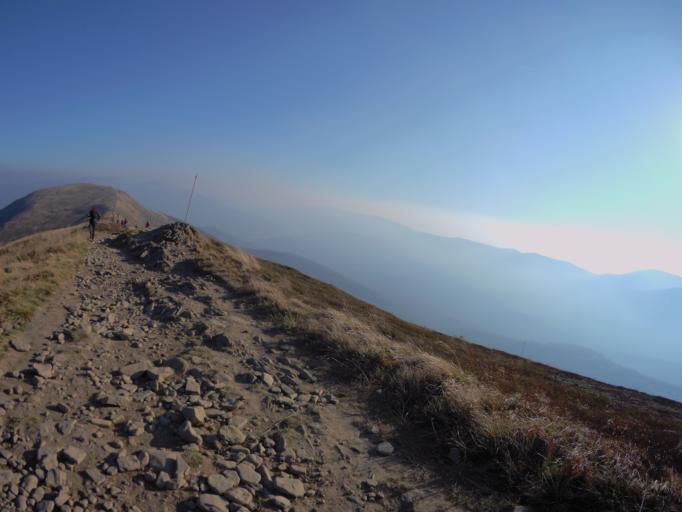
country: PL
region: Subcarpathian Voivodeship
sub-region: Powiat bieszczadzki
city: Lutowiska
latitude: 49.1356
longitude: 22.6073
